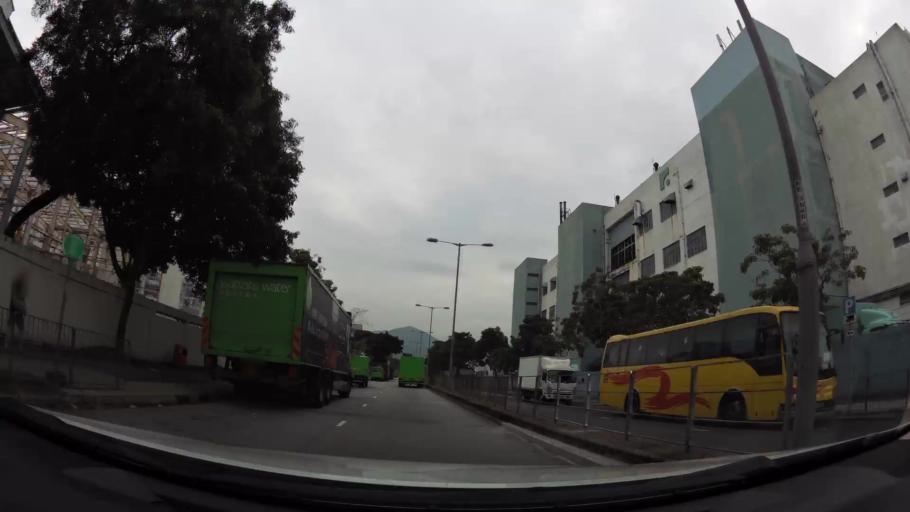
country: HK
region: Tai Po
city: Tai Po
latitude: 22.4611
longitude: 114.1884
